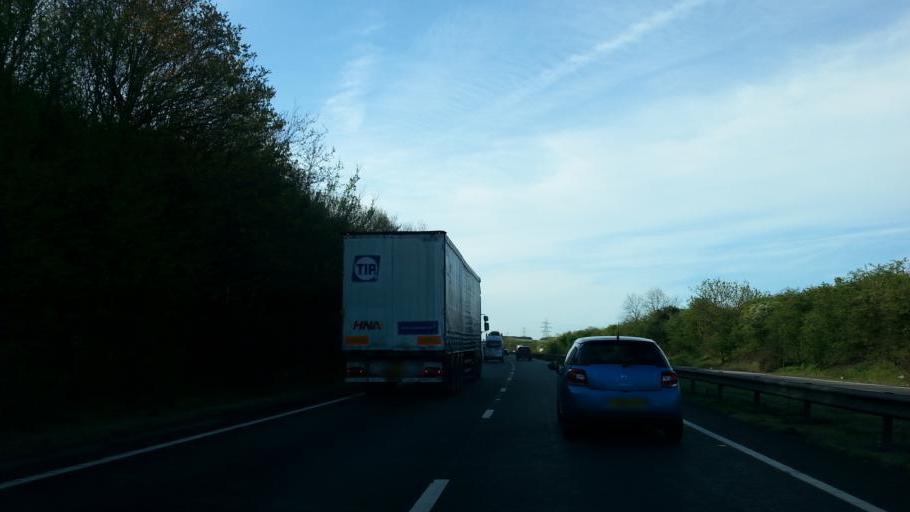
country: GB
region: England
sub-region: Lincolnshire
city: Great Gonerby
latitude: 52.9362
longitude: -0.6852
